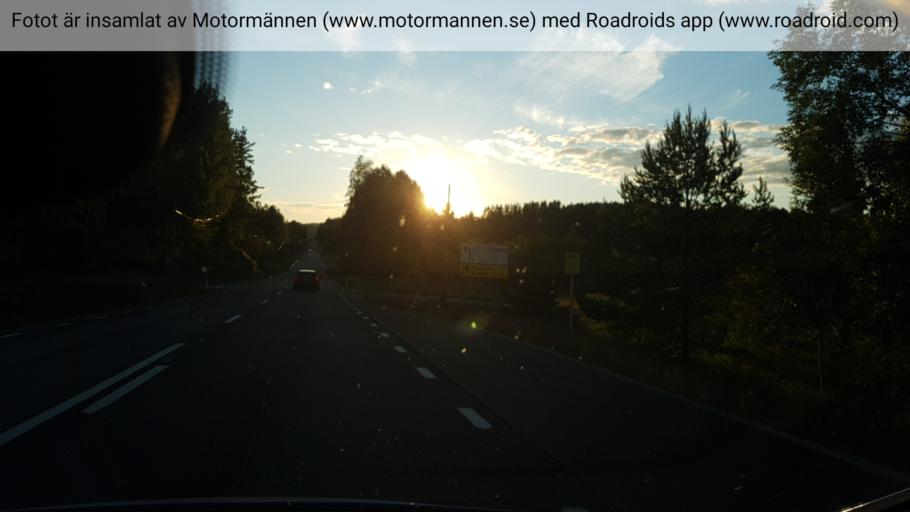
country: SE
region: Vaermland
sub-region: Sunne Kommun
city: Sunne
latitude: 59.6606
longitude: 12.9295
